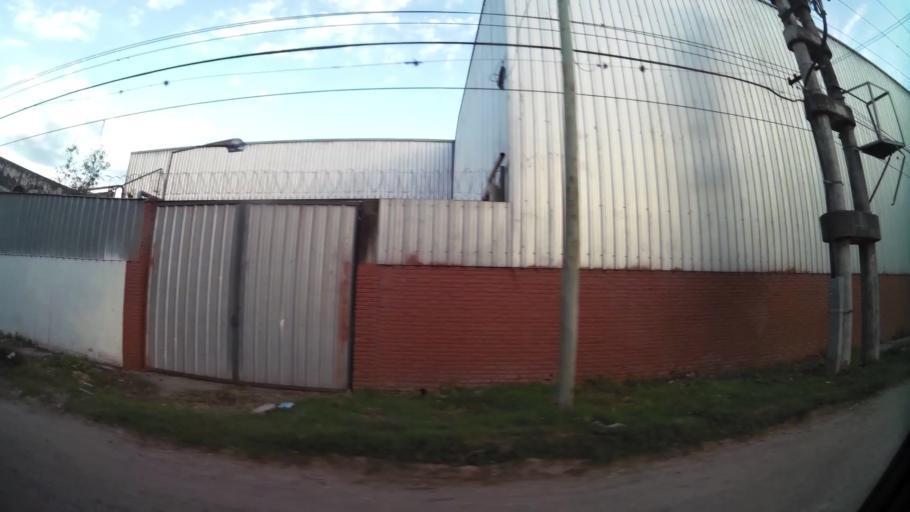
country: AR
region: Buenos Aires
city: Santa Catalina - Dique Lujan
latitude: -34.4510
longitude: -58.6631
